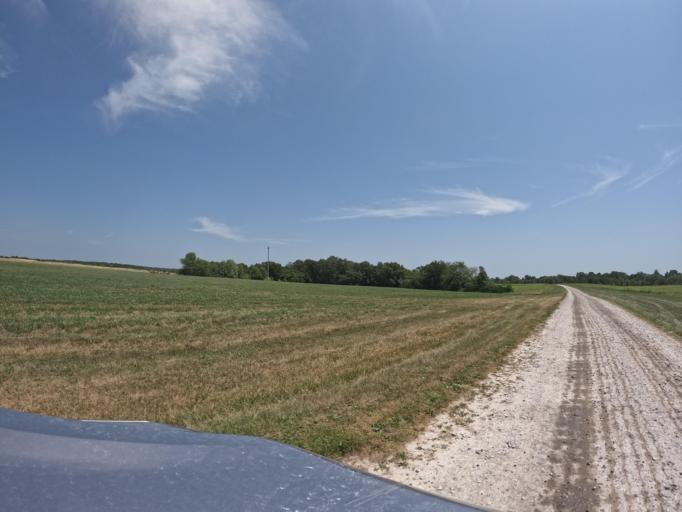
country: US
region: Iowa
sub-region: Henry County
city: Mount Pleasant
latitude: 40.9410
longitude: -91.5870
